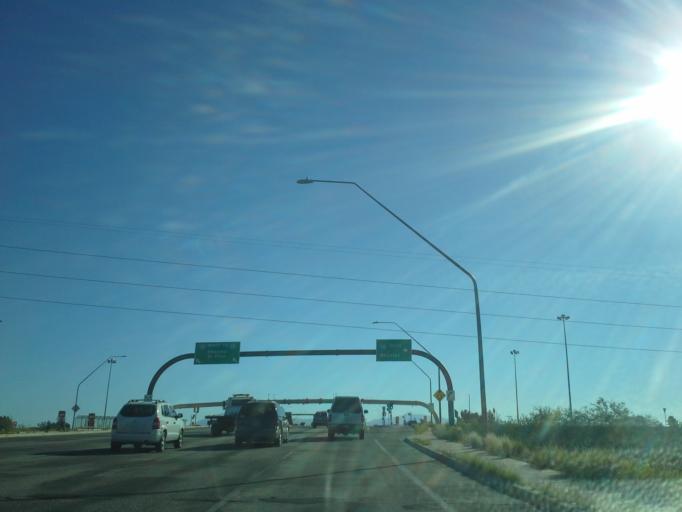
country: US
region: Arizona
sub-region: Pima County
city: Drexel Heights
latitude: 32.1338
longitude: -110.9886
